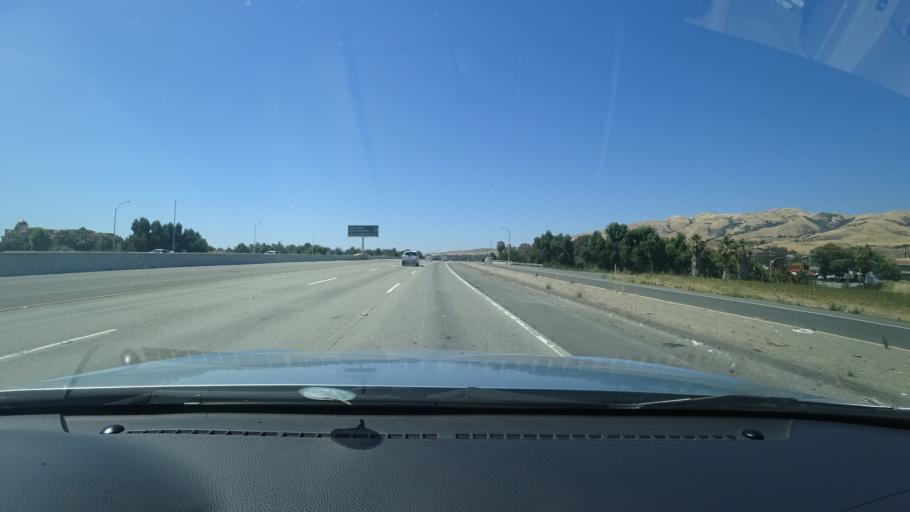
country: US
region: California
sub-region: Santa Clara County
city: Milpitas
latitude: 37.4335
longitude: -121.8877
